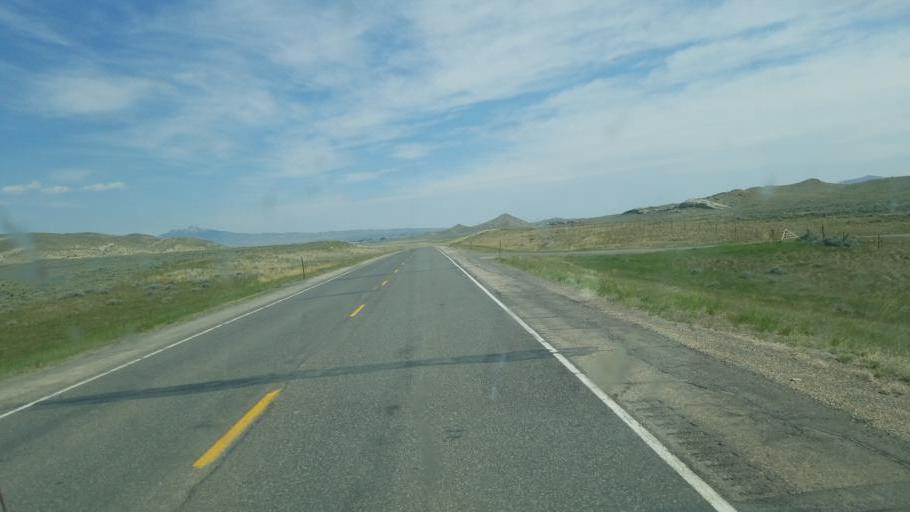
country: US
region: Wyoming
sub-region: Park County
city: Cody
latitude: 44.4587
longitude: -109.0164
